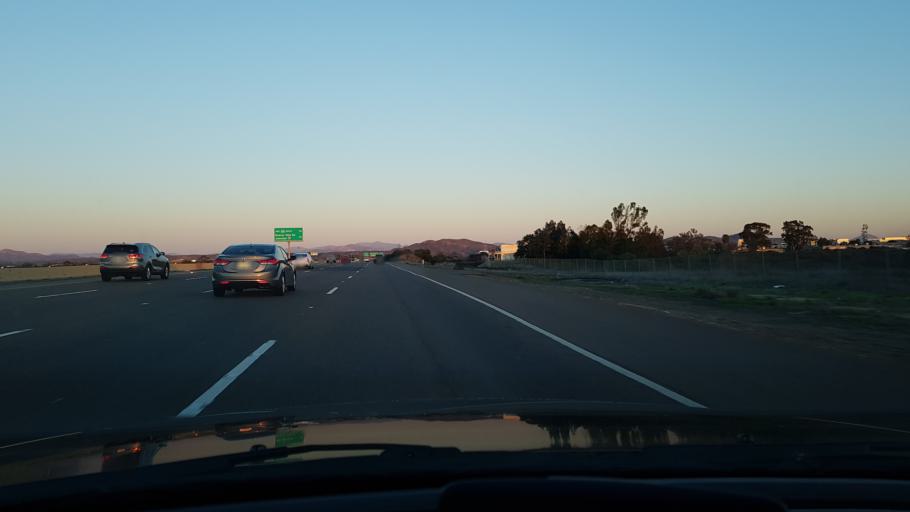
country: US
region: California
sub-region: San Diego County
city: San Diego
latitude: 32.8392
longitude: -117.1445
